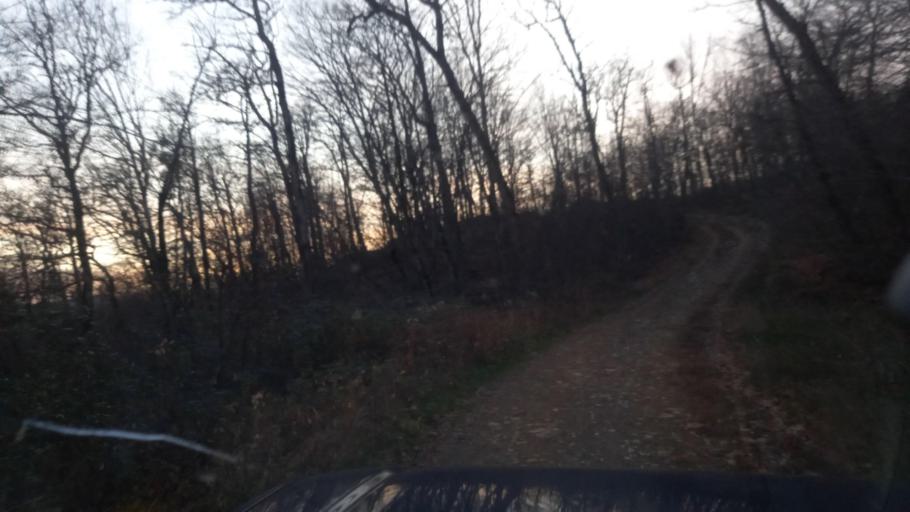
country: RU
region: Krasnodarskiy
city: Nebug
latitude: 44.3795
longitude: 39.1394
